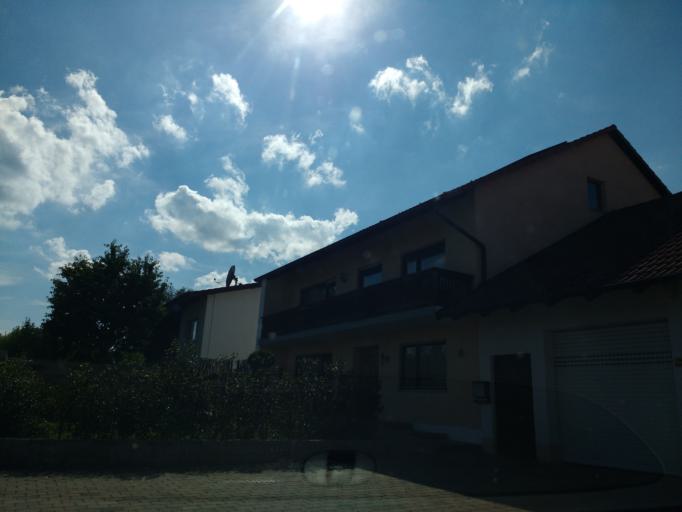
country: DE
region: Bavaria
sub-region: Upper Bavaria
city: Taufkirchen
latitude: 48.1481
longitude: 12.4544
